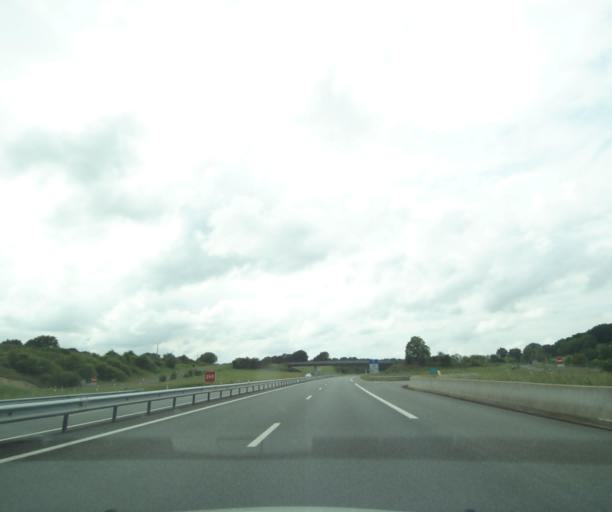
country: FR
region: Centre
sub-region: Departement du Cher
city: Orval
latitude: 46.7235
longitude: 2.4408
